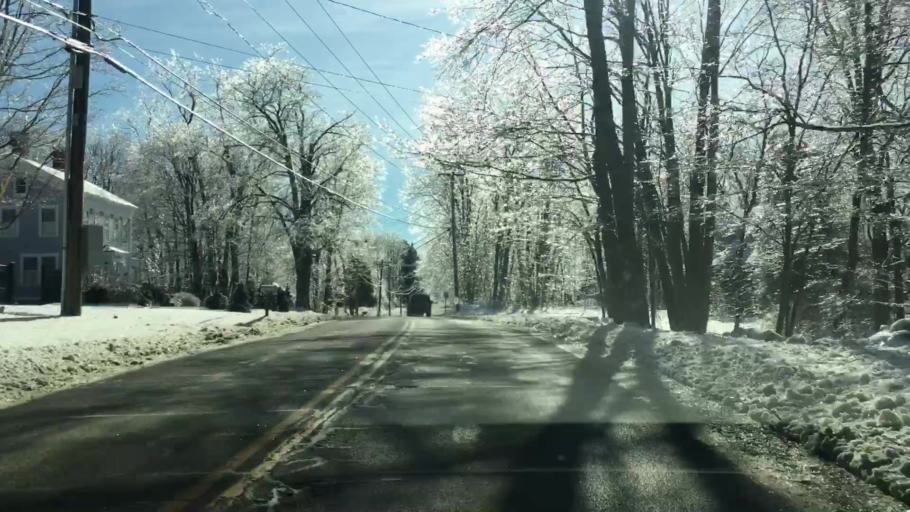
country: US
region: Connecticut
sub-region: Fairfield County
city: Newtown
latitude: 41.3897
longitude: -73.2586
